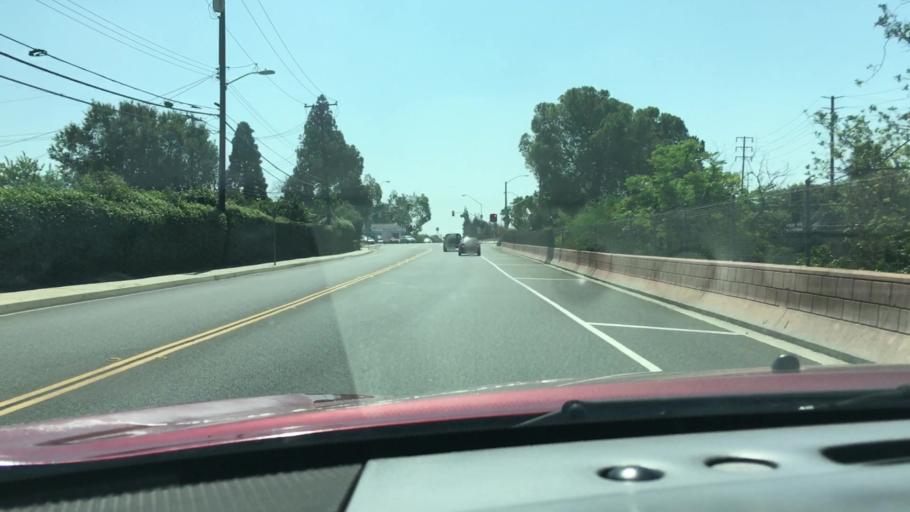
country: US
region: California
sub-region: Los Angeles County
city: La Mirada
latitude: 33.8917
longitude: -118.0155
